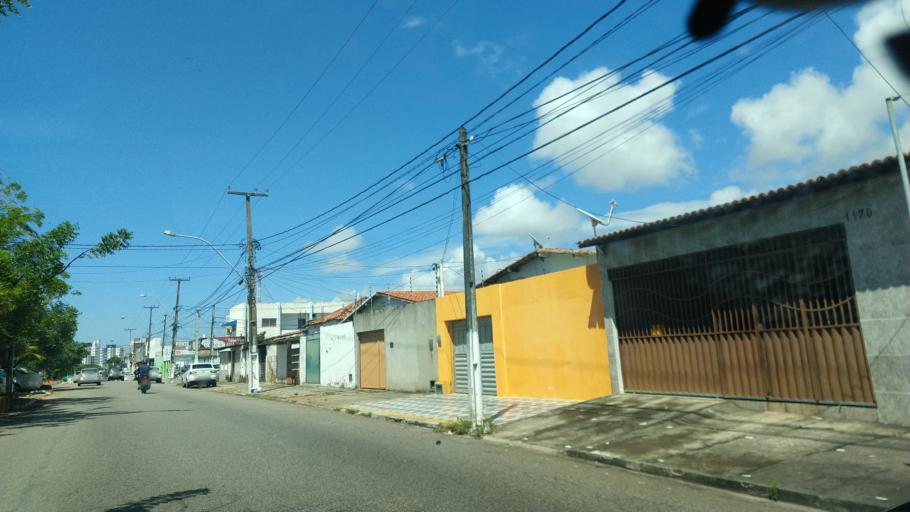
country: BR
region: Rio Grande do Norte
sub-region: Natal
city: Natal
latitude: -5.8067
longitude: -35.2127
